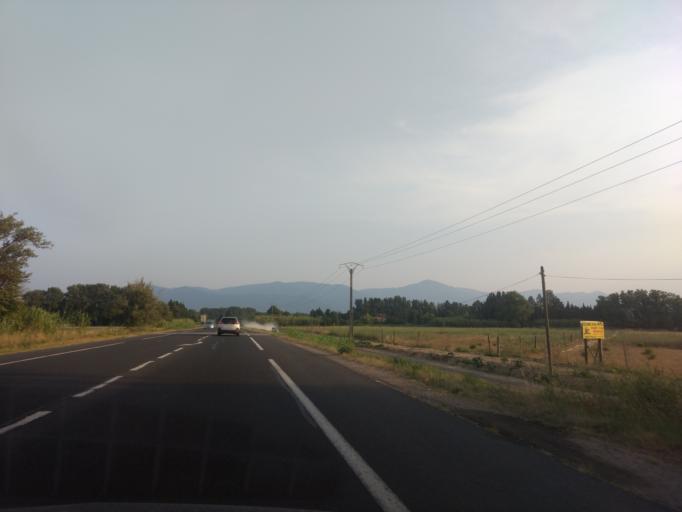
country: FR
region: Languedoc-Roussillon
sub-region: Departement des Pyrenees-Orientales
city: Latour-Bas-Elne
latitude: 42.6060
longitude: 3.0244
